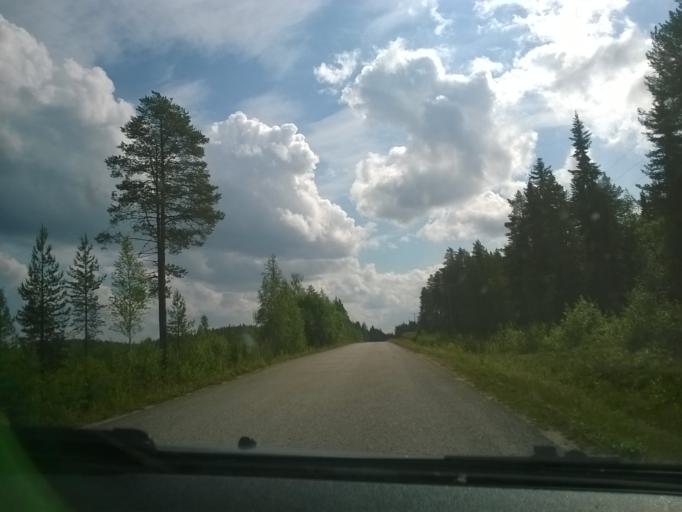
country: FI
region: Kainuu
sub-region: Kehys-Kainuu
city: Kuhmo
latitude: 64.4251
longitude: 29.7442
